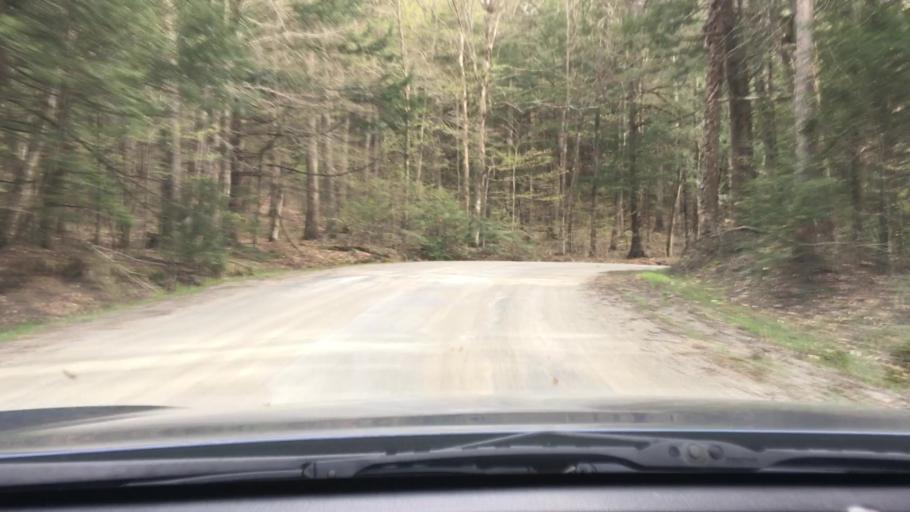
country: US
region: New York
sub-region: Essex County
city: Ticonderoga
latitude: 43.8186
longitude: -73.7400
